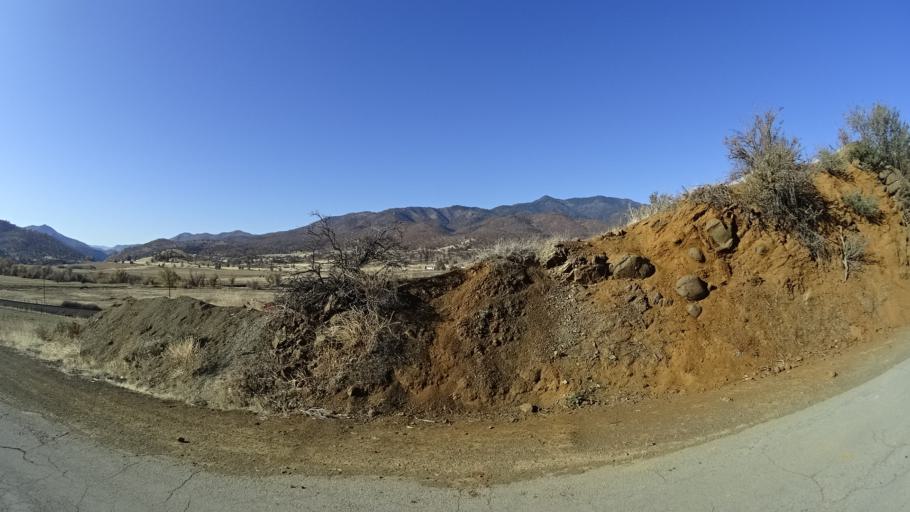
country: US
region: California
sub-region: Siskiyou County
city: Montague
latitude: 41.9000
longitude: -122.5443
